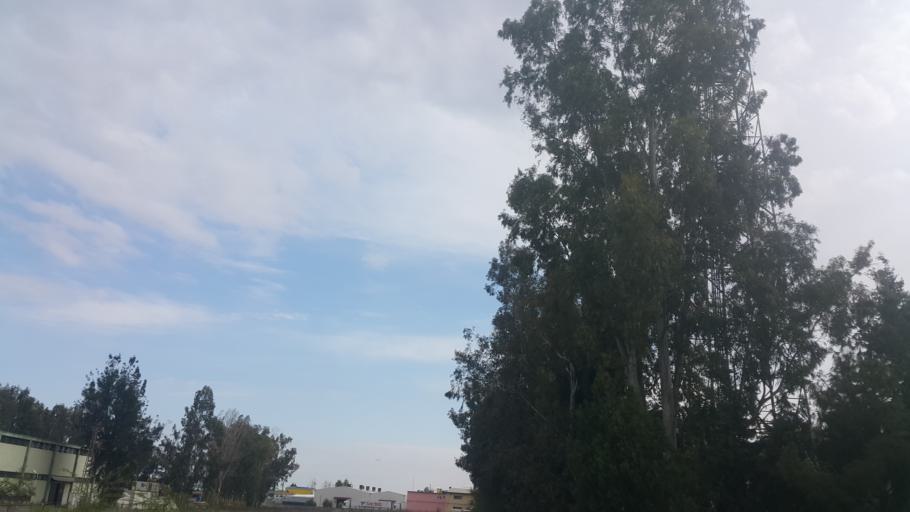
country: TR
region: Adana
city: Seyhan
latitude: 36.9943
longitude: 35.2089
